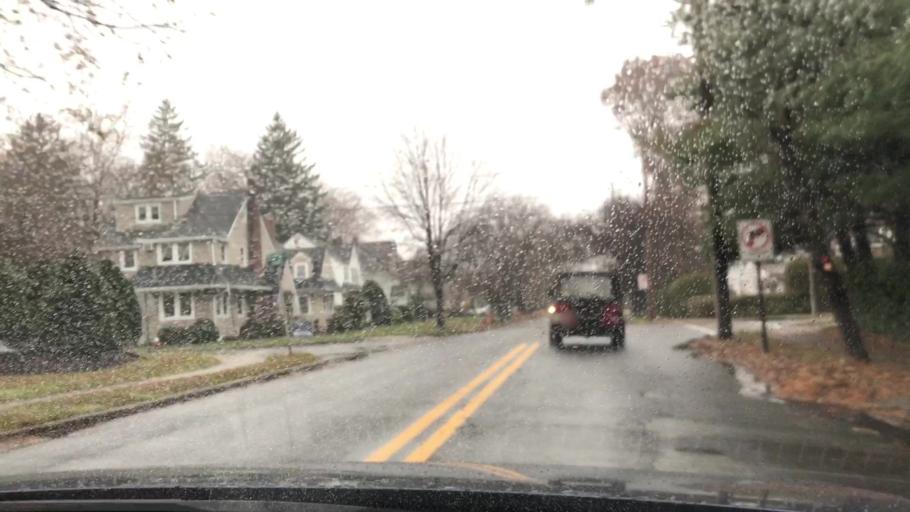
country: US
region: New Jersey
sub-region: Bergen County
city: Ho-Ho-Kus
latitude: 40.9808
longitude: -74.0954
